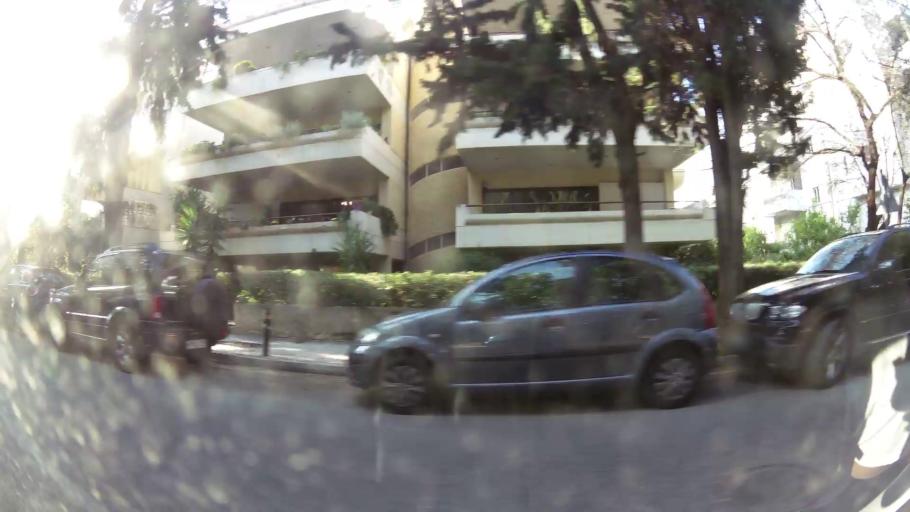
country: GR
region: Attica
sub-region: Nomarchia Athinas
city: Agia Paraskevi
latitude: 38.0057
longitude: 23.8329
